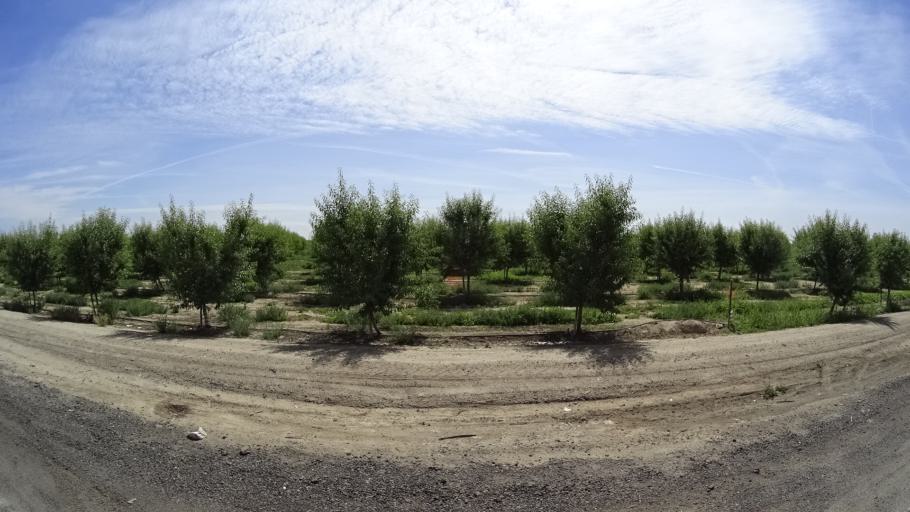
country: US
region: California
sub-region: Kings County
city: Hanford
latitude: 36.3384
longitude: -119.6235
